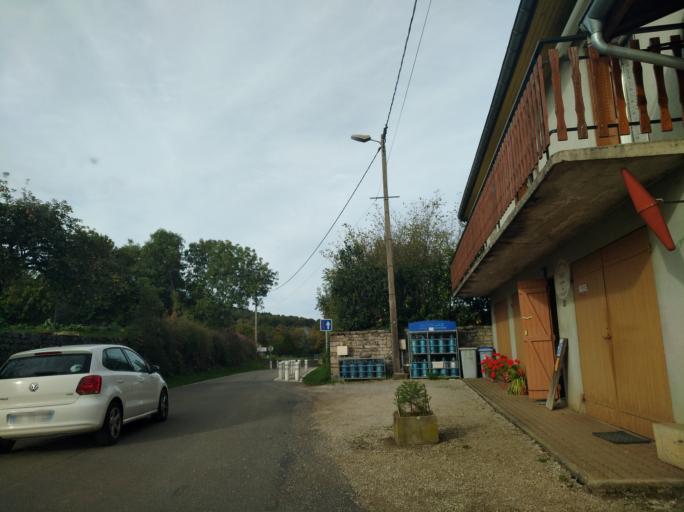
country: FR
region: Bourgogne
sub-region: Departement de Saone-et-Loire
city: Cuiseaux
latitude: 46.4779
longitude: 5.4555
